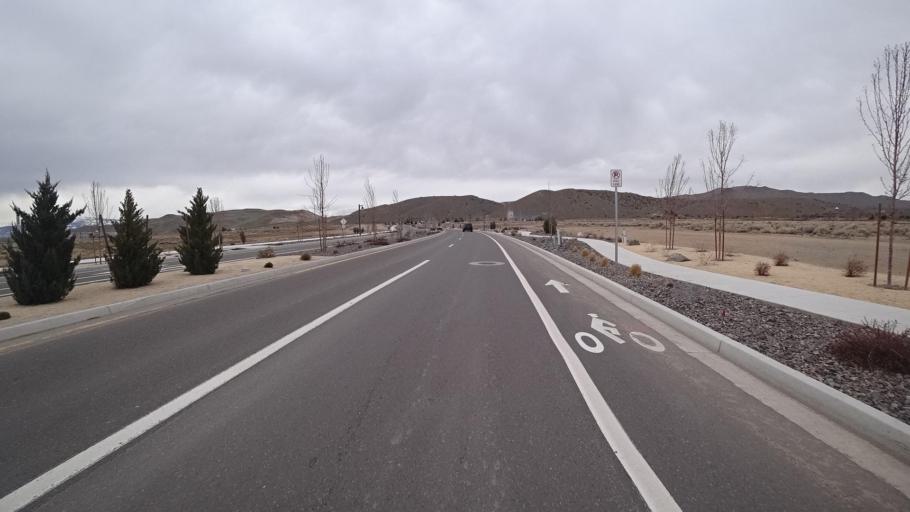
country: US
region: Nevada
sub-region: Washoe County
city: Spanish Springs
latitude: 39.6154
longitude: -119.7192
